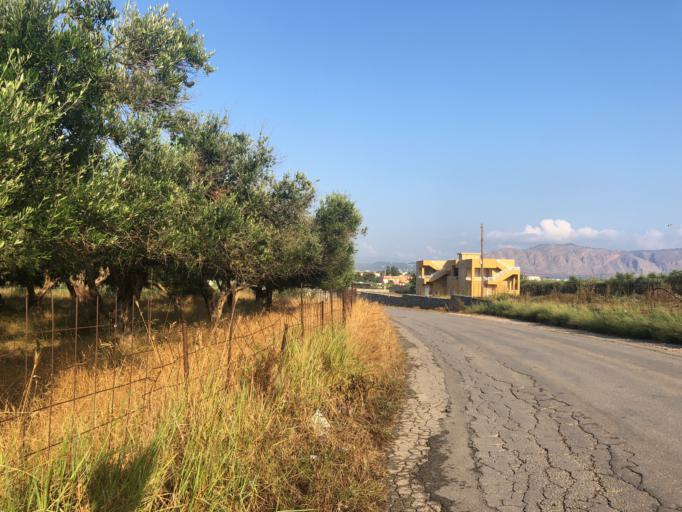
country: GR
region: Crete
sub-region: Nomos Chanias
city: Georgioupolis
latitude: 35.3480
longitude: 24.3070
